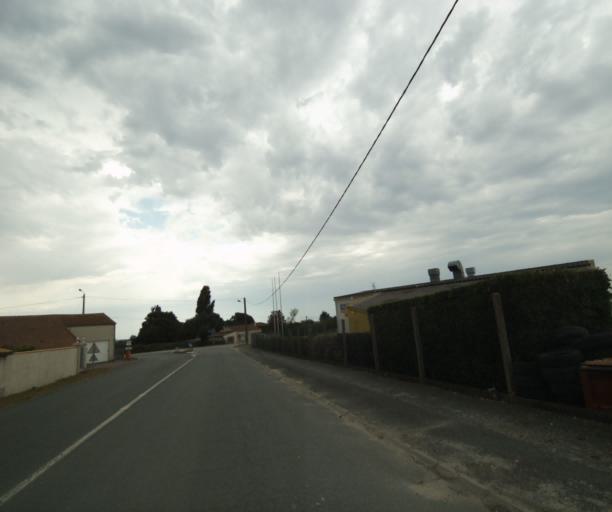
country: FR
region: Poitou-Charentes
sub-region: Departement de la Charente-Maritime
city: Tonnay-Charente
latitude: 45.9525
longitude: -0.8875
